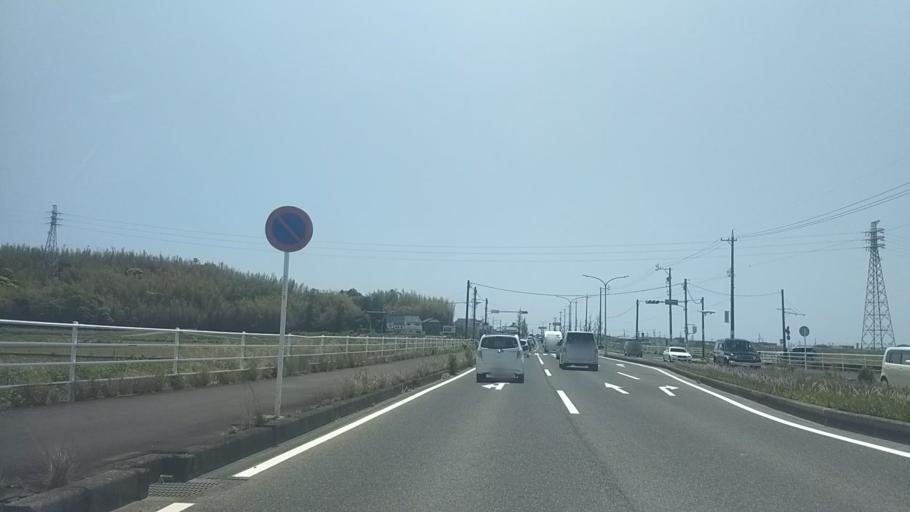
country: JP
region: Shizuoka
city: Hamamatsu
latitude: 34.7057
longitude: 137.6488
